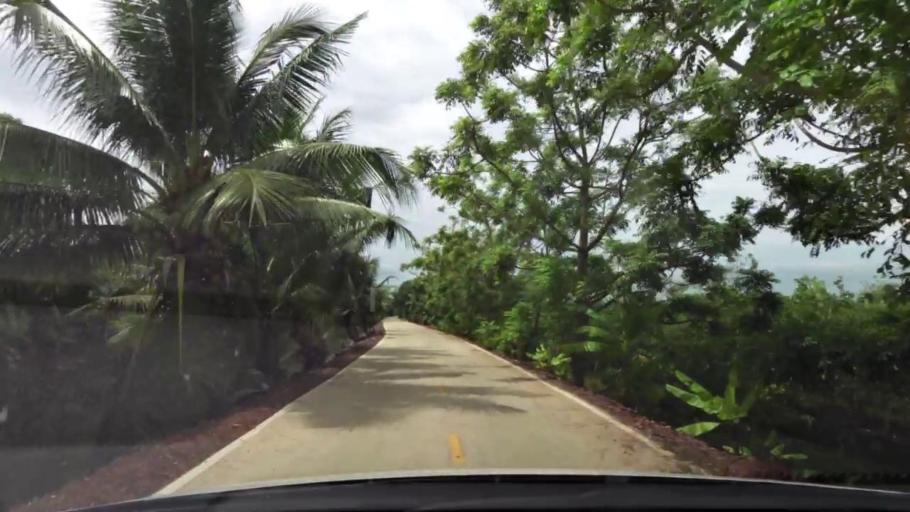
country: TH
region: Ratchaburi
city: Damnoen Saduak
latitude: 13.5523
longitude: 99.9821
